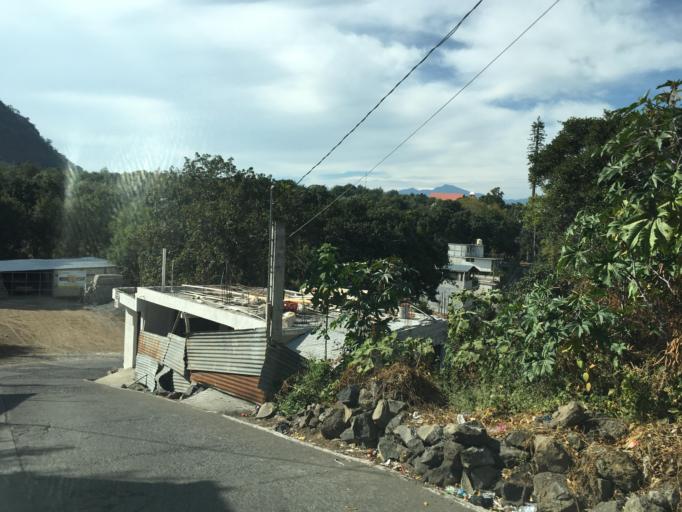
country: GT
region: Solola
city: San Antonio Palopo
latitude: 14.6672
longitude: -91.1660
